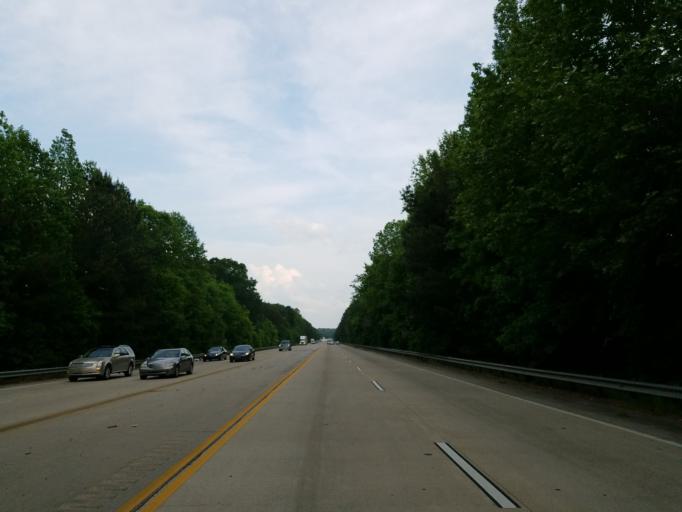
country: US
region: Georgia
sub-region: Cobb County
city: Powder Springs
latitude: 33.8292
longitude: -84.6686
